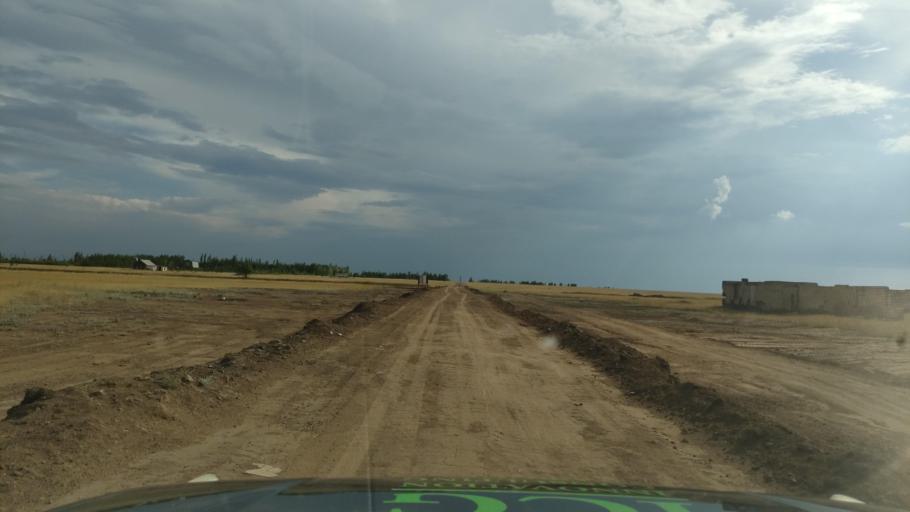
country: KZ
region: Pavlodar
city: Pavlodar
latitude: 52.5139
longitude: 77.4393
